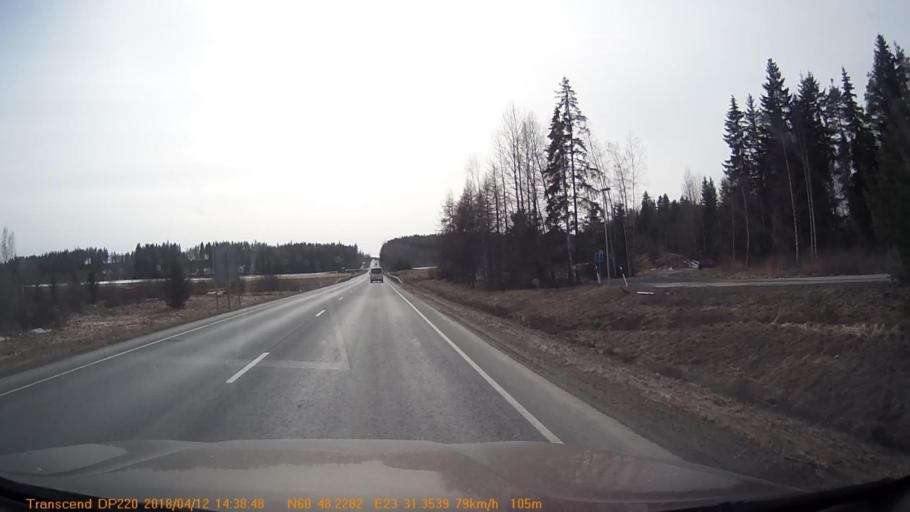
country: FI
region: Haeme
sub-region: Forssa
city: Jokioinen
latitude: 60.8026
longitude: 23.5204
